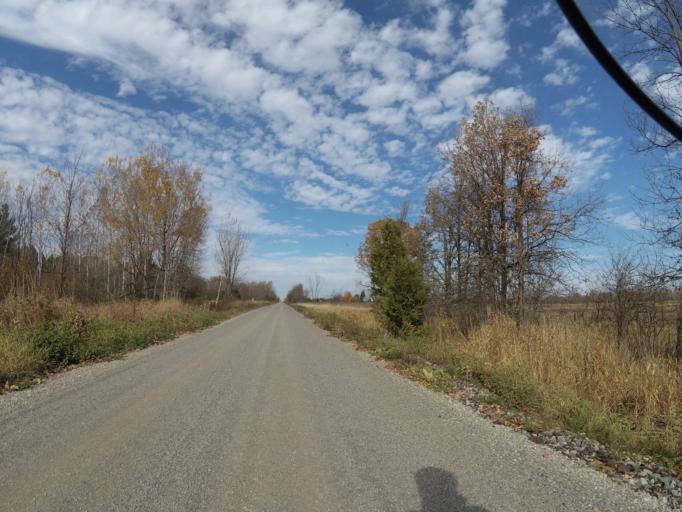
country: CA
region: Ontario
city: Carleton Place
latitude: 45.0380
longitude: -76.0833
